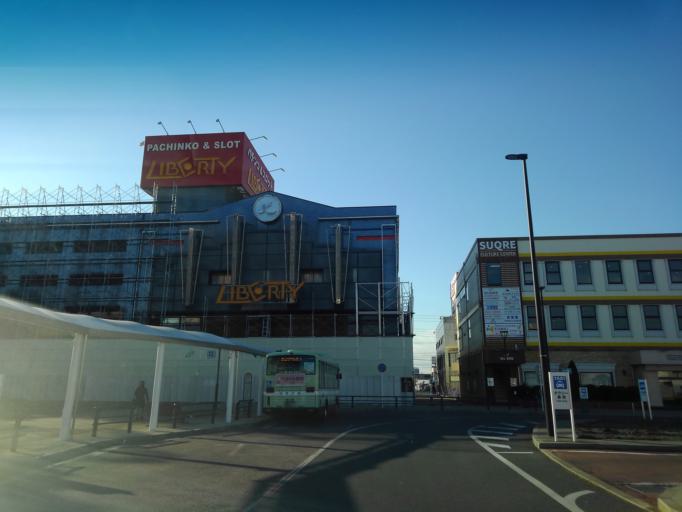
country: JP
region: Chiba
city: Kimitsu
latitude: 35.3347
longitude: 139.8950
